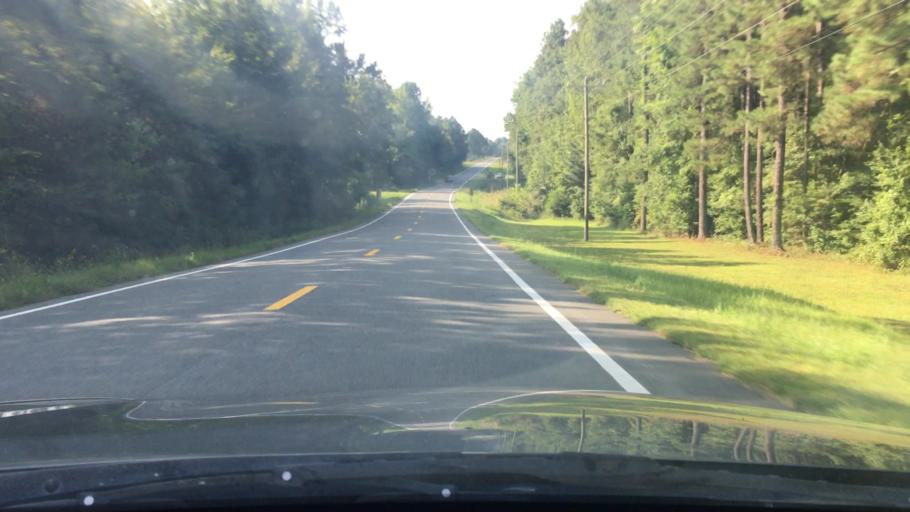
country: US
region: North Carolina
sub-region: Alamance County
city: Green Level
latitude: 36.2221
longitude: -79.3226
